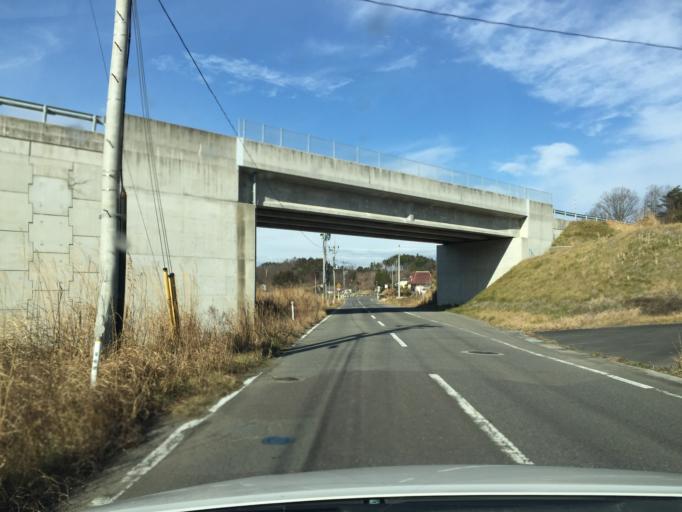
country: JP
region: Fukushima
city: Ishikawa
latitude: 37.2546
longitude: 140.5638
